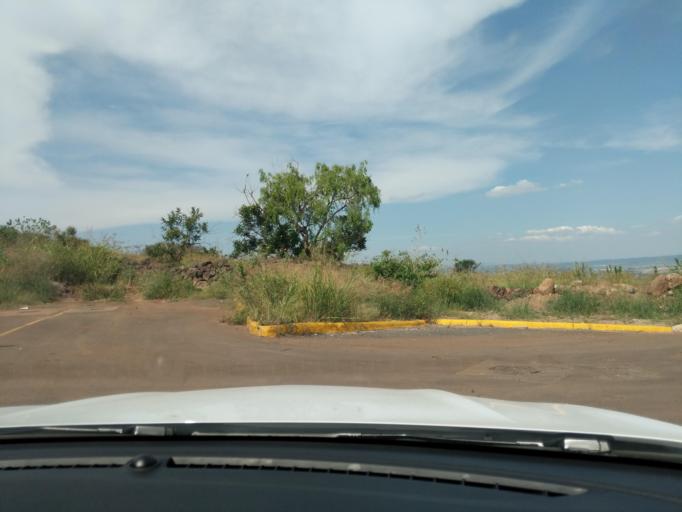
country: MX
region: Jalisco
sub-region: El Salto
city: El Muey
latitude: 20.5223
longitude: -103.2188
